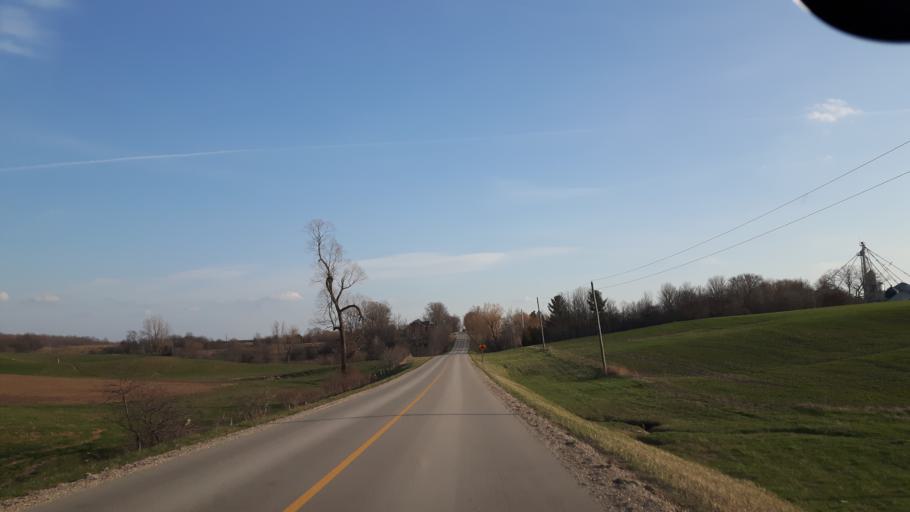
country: CA
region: Ontario
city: Goderich
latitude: 43.6470
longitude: -81.6643
